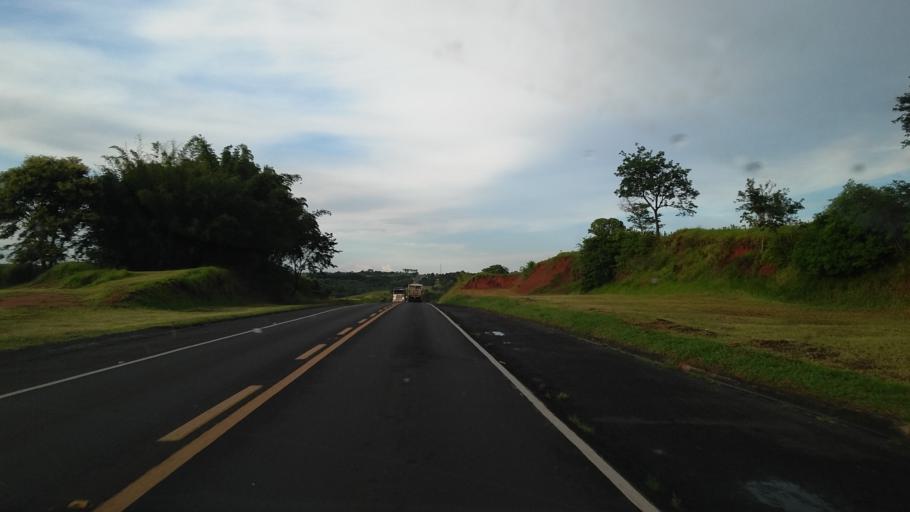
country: BR
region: Sao Paulo
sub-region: Marilia
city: Marilia
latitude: -21.9392
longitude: -49.9200
